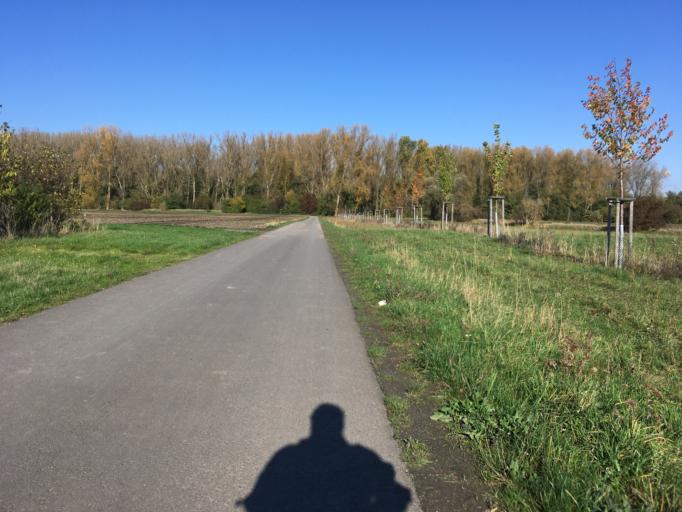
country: DE
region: Hesse
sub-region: Regierungsbezirk Darmstadt
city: Biblis
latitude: 49.6727
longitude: 8.4430
